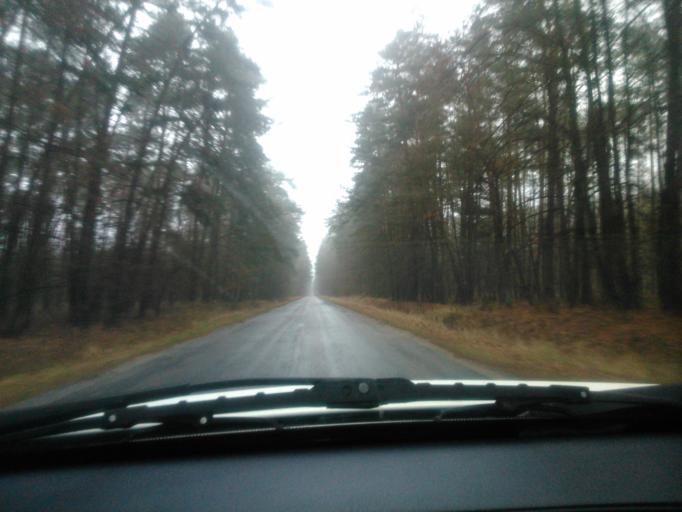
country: PL
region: Kujawsko-Pomorskie
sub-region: Powiat wabrzeski
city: Debowa Laka
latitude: 53.1791
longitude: 19.1436
